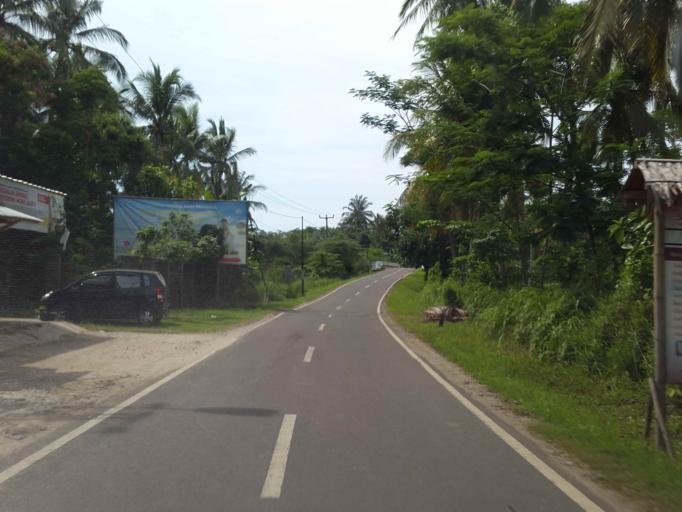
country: ID
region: Banten
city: Citeureup
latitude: -6.5236
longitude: 105.6891
